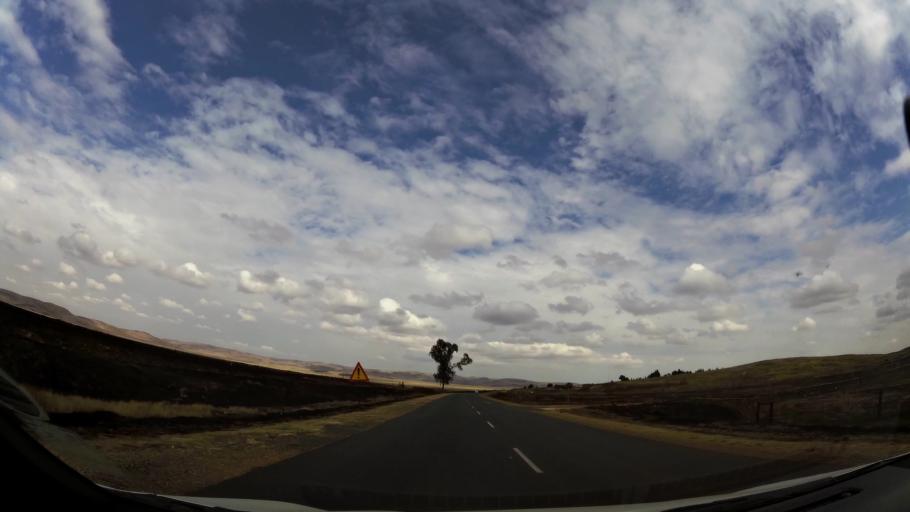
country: ZA
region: Gauteng
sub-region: Sedibeng District Municipality
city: Heidelberg
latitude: -26.4206
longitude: 28.2713
